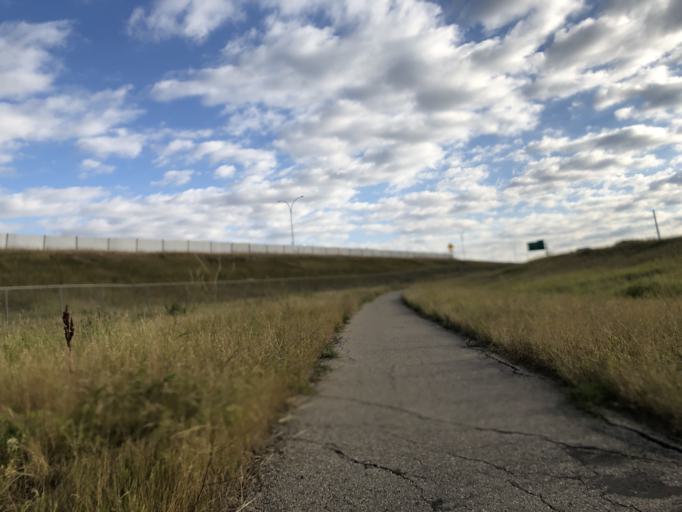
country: CA
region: Alberta
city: Calgary
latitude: 51.0080
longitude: -114.0150
